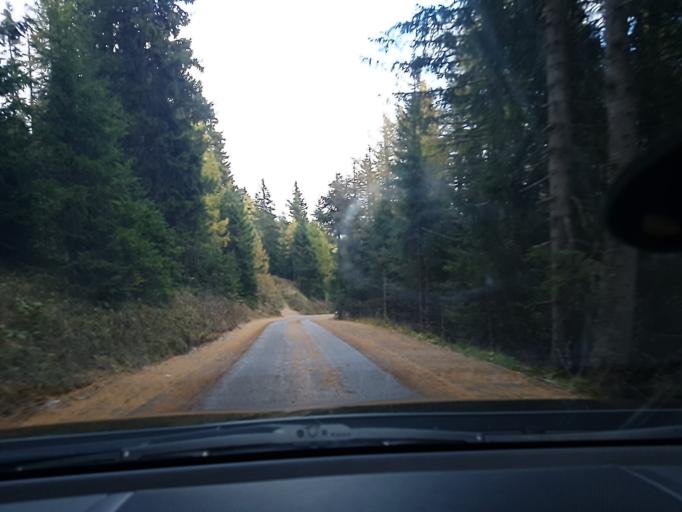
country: AT
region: Styria
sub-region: Politischer Bezirk Murtal
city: Oberzeiring
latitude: 47.2646
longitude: 14.4371
